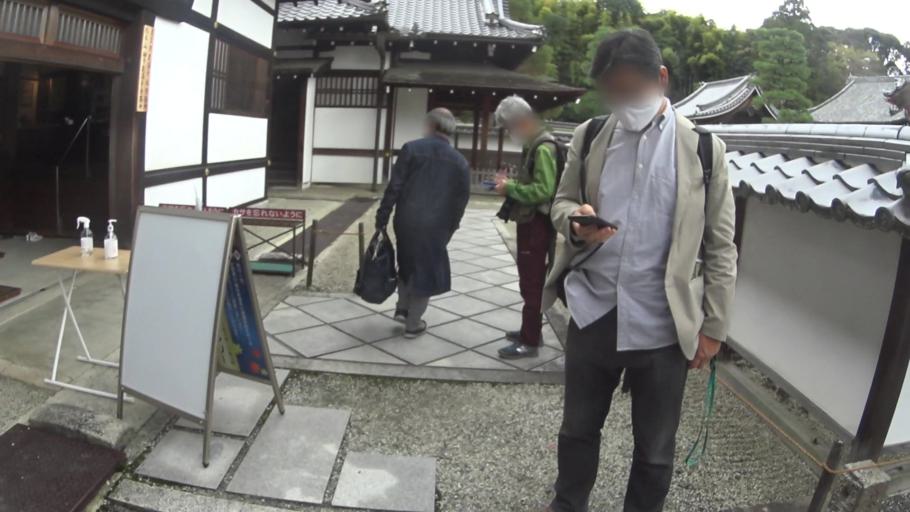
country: JP
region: Kyoto
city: Kyoto
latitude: 34.9780
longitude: 135.7816
